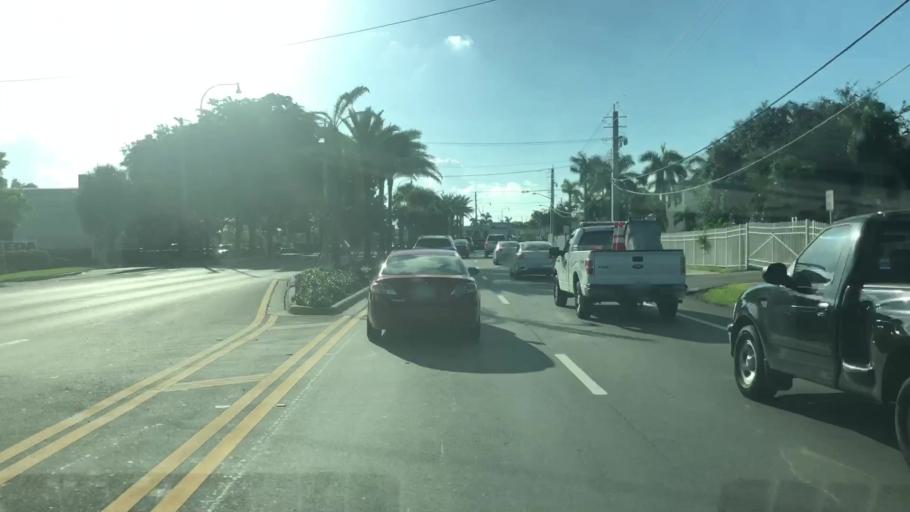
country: US
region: Florida
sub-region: Broward County
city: Coconut Creek
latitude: 26.2450
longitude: -80.1550
